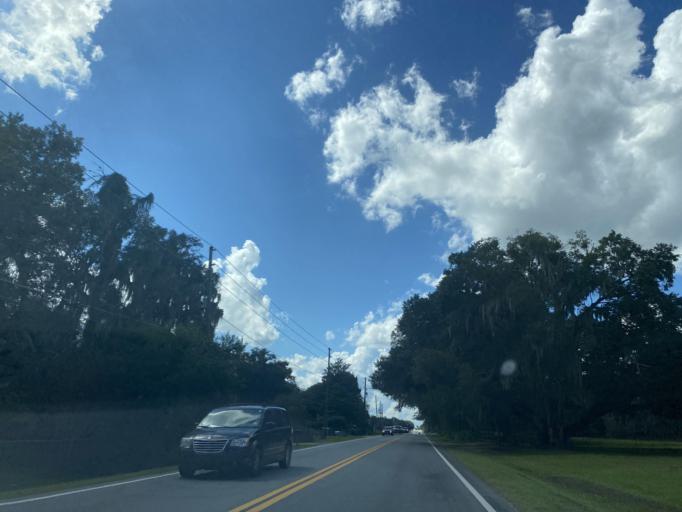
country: US
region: Florida
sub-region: Sumter County
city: The Villages
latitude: 28.9820
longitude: -81.9835
